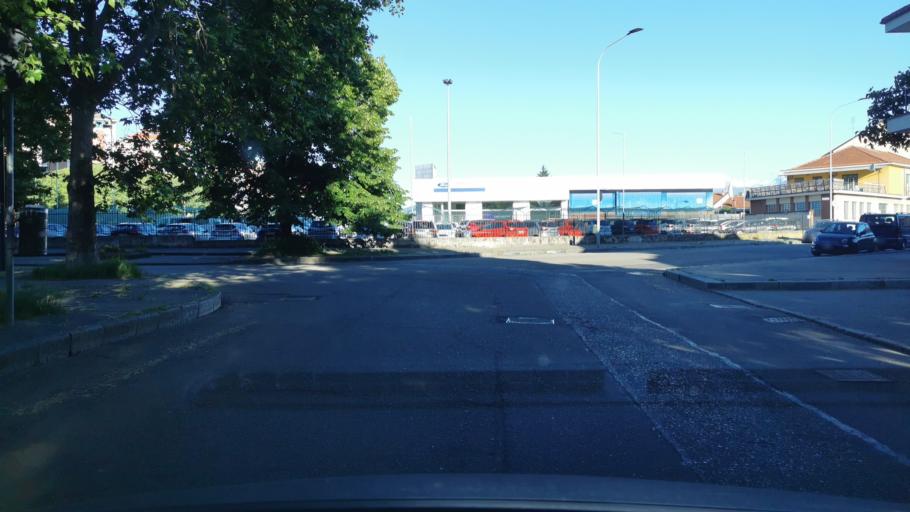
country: IT
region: Piedmont
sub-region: Provincia di Torino
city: Venaria Reale
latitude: 45.1064
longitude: 7.6550
